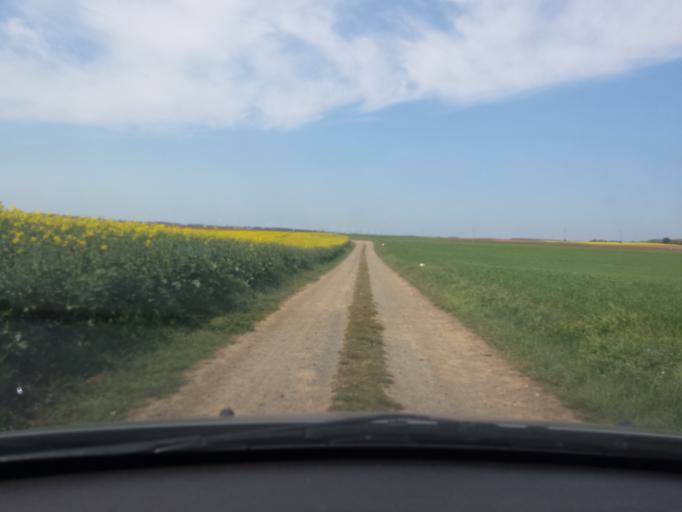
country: FR
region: Pays de la Loire
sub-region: Departement de la Vendee
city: Sainte-Gemme-la-Plaine
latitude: 46.4900
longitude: -1.0810
